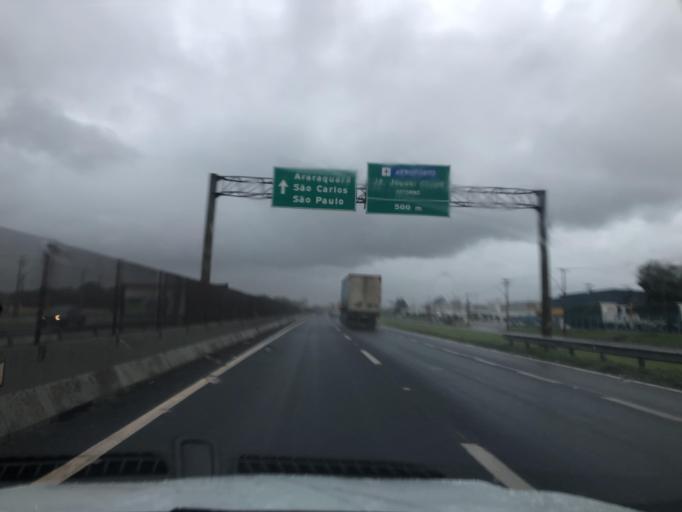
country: BR
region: Sao Paulo
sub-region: Ribeirao Preto
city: Ribeirao Preto
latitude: -21.1407
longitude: -47.7613
